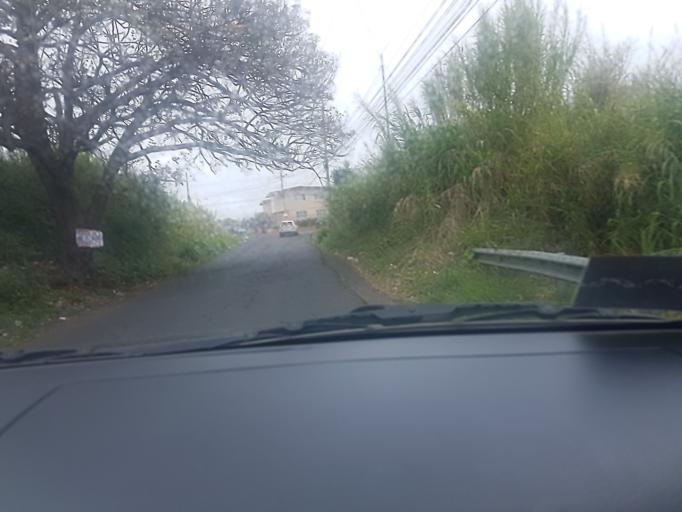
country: CR
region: San Jose
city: Calle Blancos
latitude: 9.9497
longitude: -84.0747
